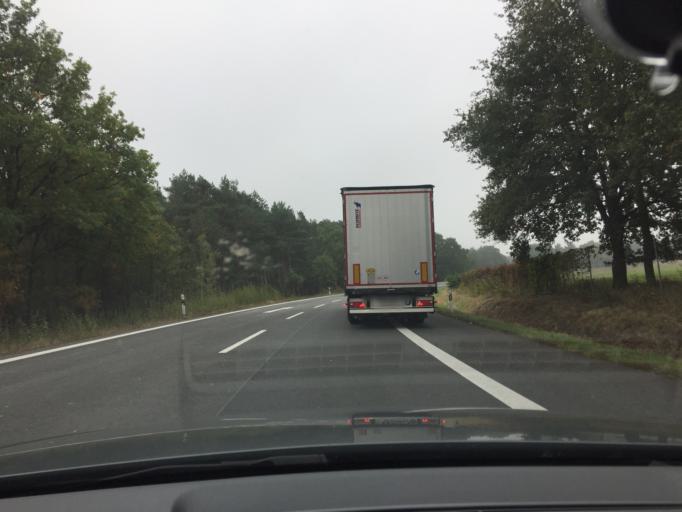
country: DE
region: Brandenburg
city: Lubbenau
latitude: 51.8445
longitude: 13.9216
